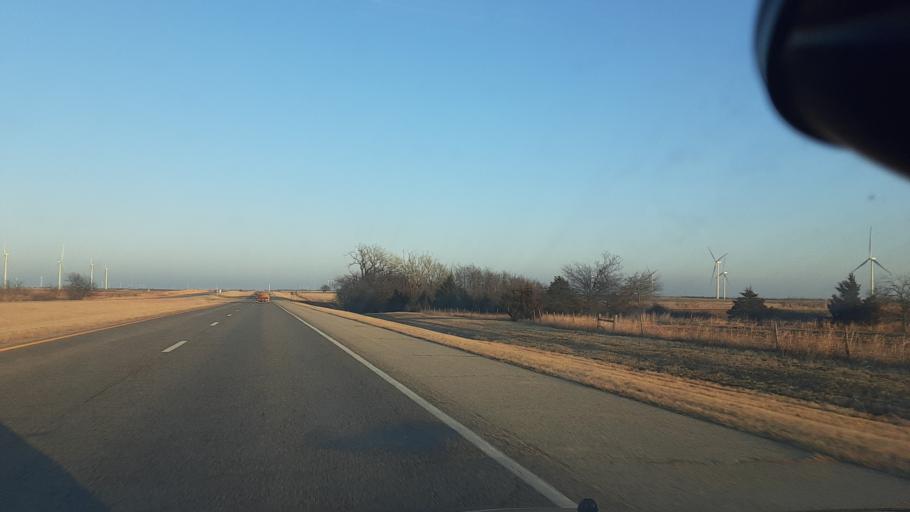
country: US
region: Oklahoma
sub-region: Noble County
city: Perry
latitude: 36.3976
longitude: -97.5173
